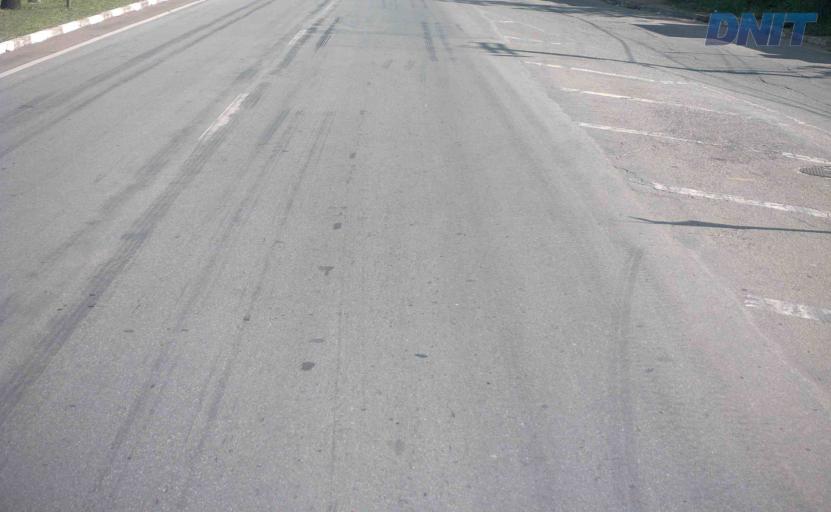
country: BR
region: Minas Gerais
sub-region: Ipatinga
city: Ipatinga
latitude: -19.4661
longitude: -42.5358
